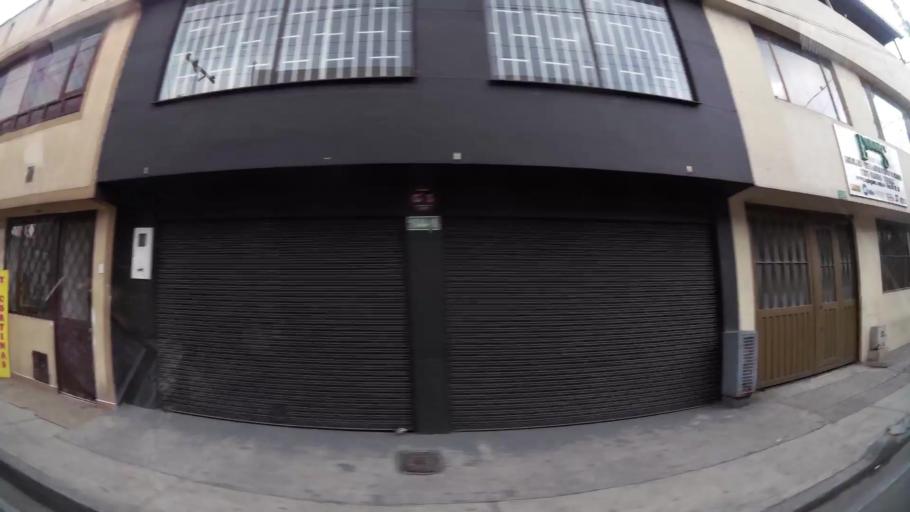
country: CO
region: Cundinamarca
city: La Calera
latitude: 4.7452
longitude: -74.0439
